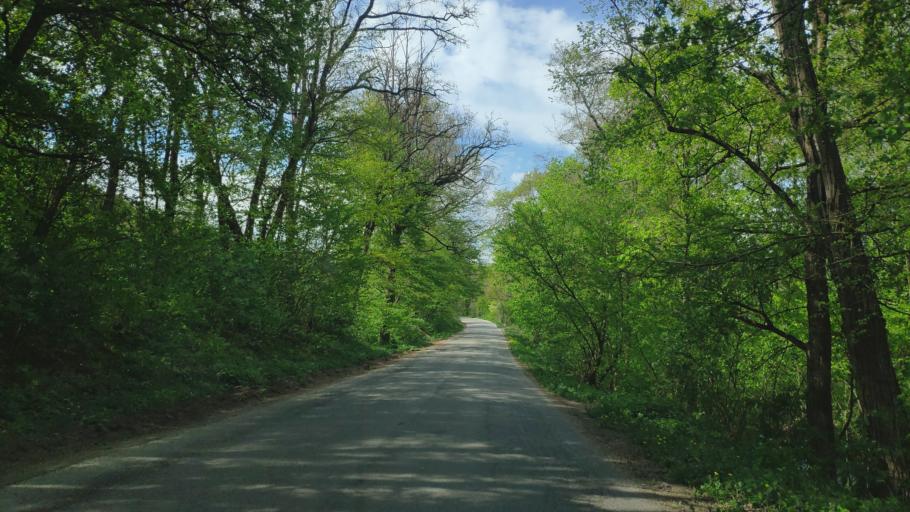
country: SK
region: Kosicky
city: Moldava nad Bodvou
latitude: 48.5873
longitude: 20.9121
